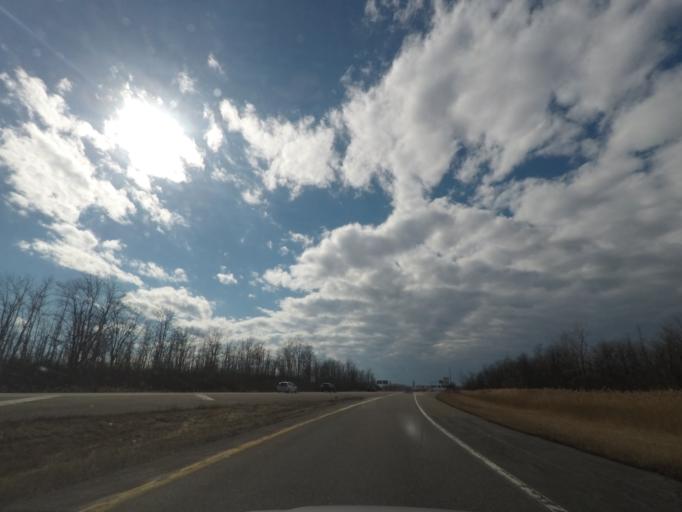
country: US
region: New York
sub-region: Onondaga County
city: East Syracuse
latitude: 43.0571
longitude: -76.0594
